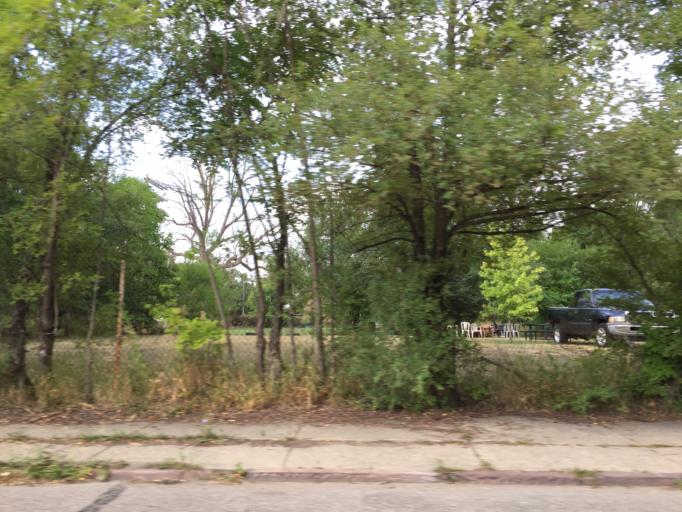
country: US
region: Michigan
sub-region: Wayne County
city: Hamtramck
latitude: 42.3648
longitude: -83.0403
